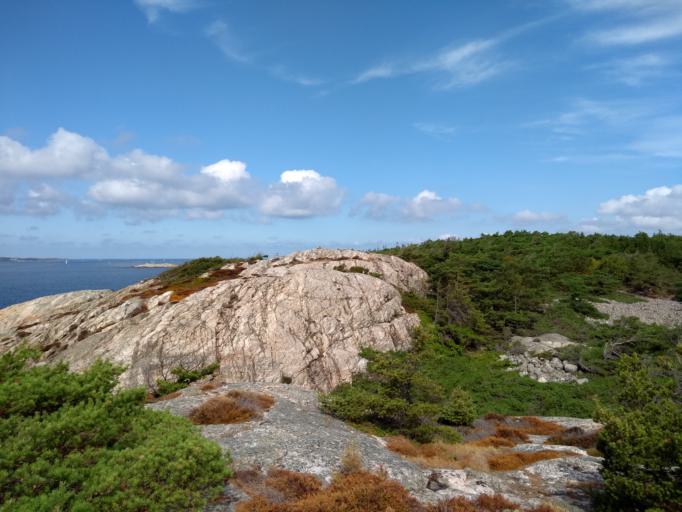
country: SE
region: Vaestra Goetaland
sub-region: Stromstads Kommun
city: Stroemstad
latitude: 58.8654
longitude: 11.1234
